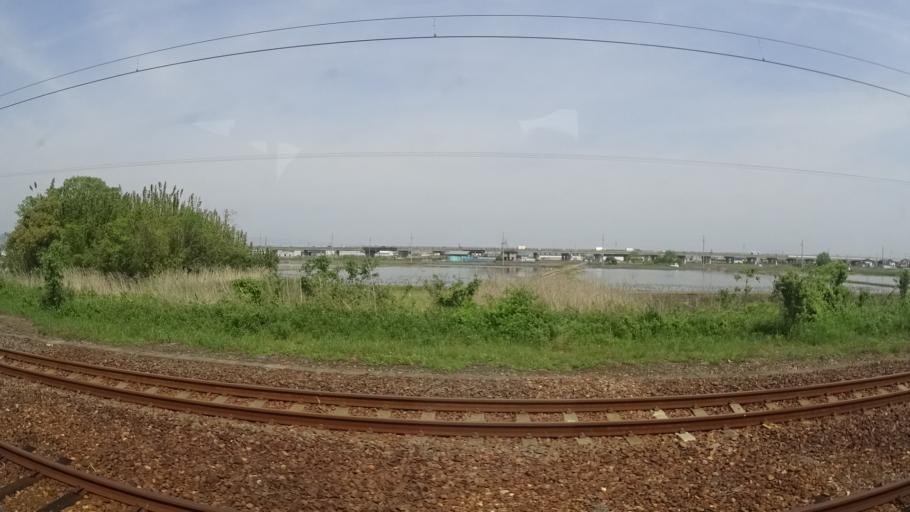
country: JP
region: Aichi
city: Kanie
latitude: 35.1333
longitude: 136.7652
